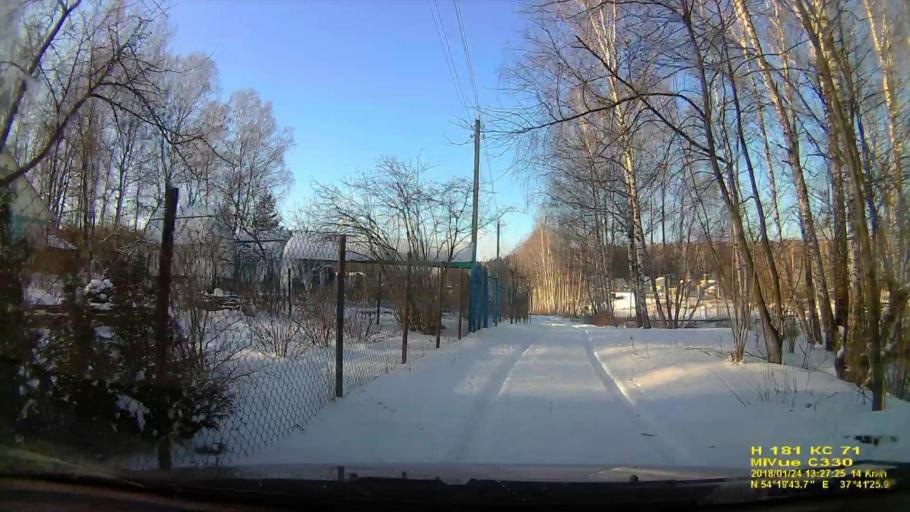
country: RU
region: Tula
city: Revyakino
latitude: 54.3289
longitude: 37.6905
